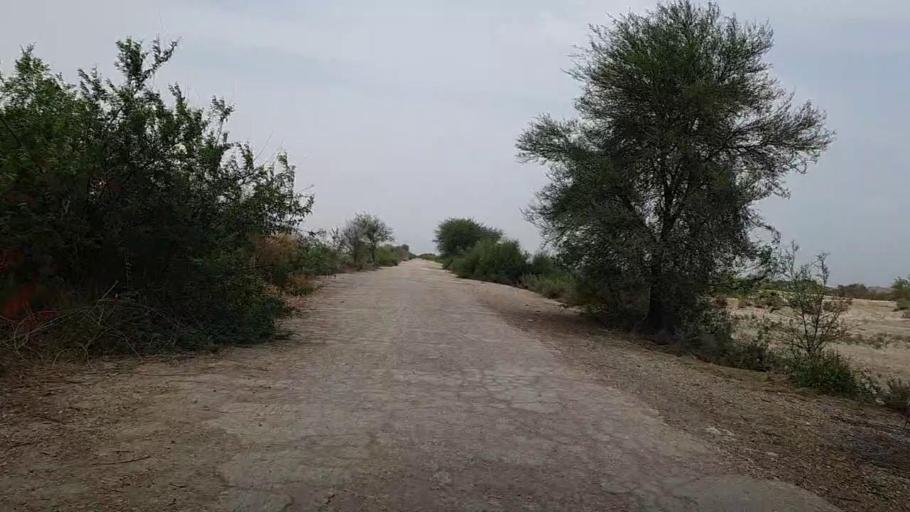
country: PK
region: Sindh
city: Sann
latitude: 26.2059
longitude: 67.9675
